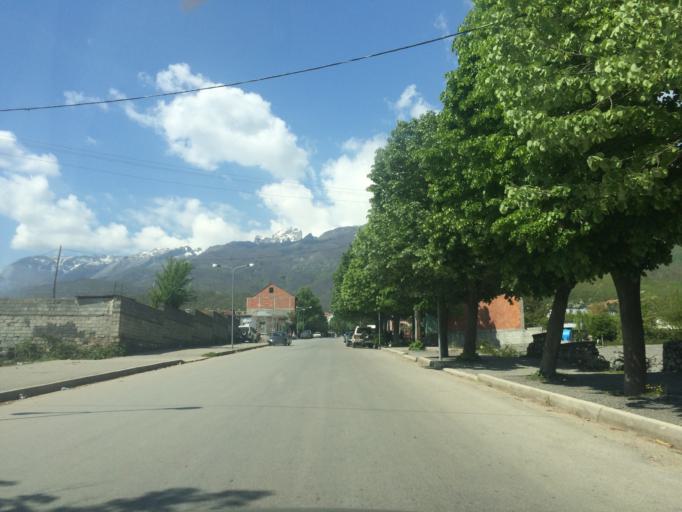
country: AL
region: Kukes
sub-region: Rrethi i Tropojes
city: Bajram Curri
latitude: 42.3568
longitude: 20.0808
